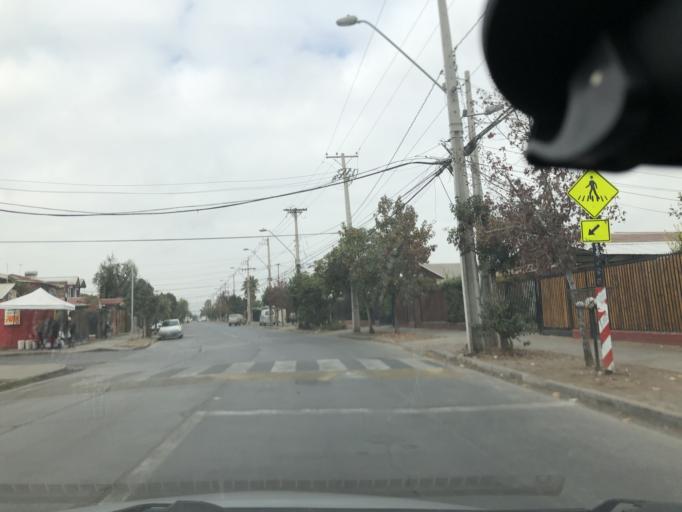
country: CL
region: Santiago Metropolitan
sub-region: Provincia de Santiago
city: La Pintana
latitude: -33.5760
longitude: -70.6041
